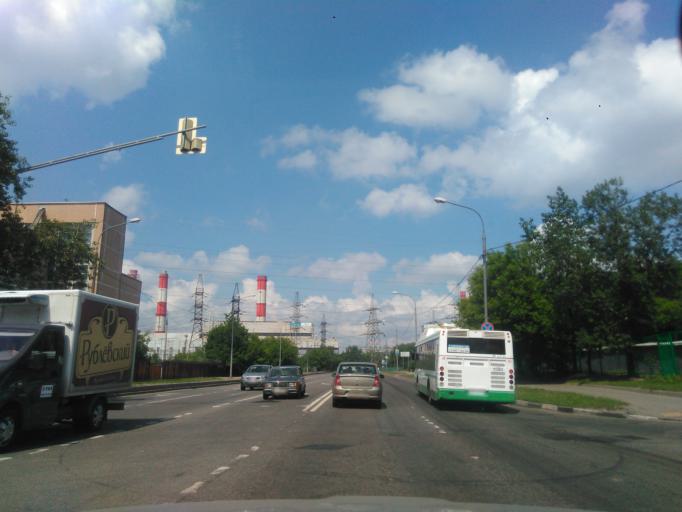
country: RU
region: Moscow
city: Businovo
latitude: 55.8874
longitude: 37.5136
